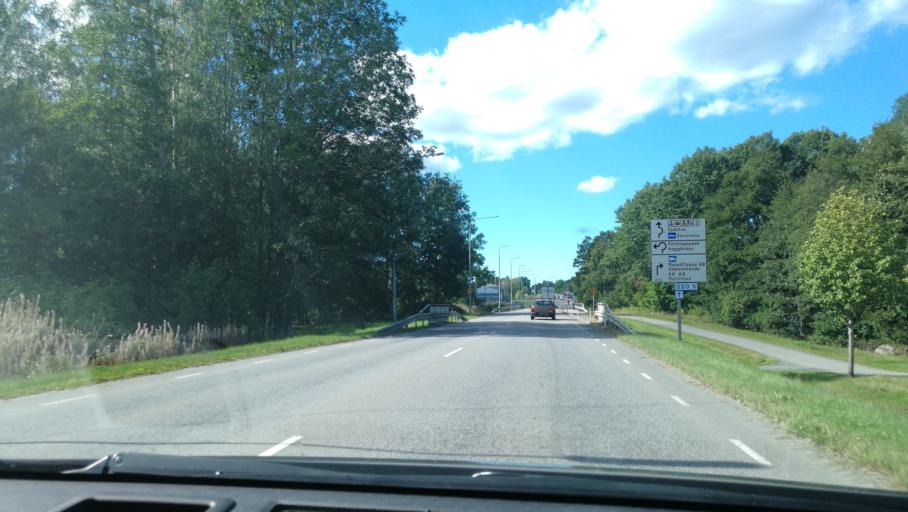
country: SE
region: Vaestra Goetaland
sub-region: Mariestads Kommun
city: Mariestad
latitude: 58.6922
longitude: 13.8271
